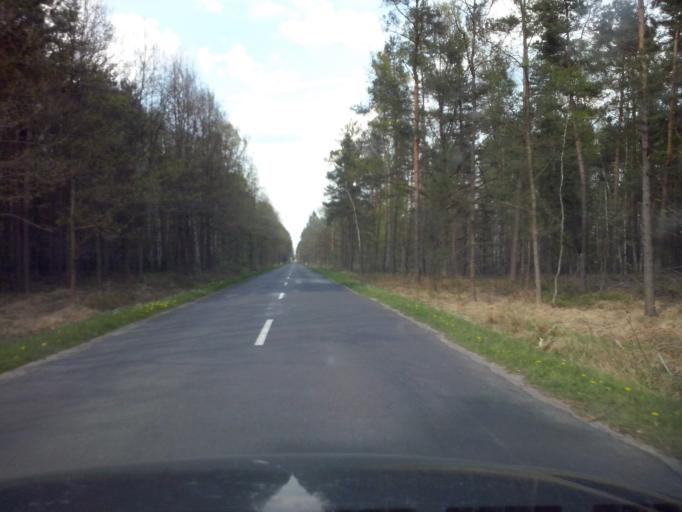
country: PL
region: Subcarpathian Voivodeship
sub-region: Powiat lezajski
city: Letownia
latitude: 50.3674
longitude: 22.2474
